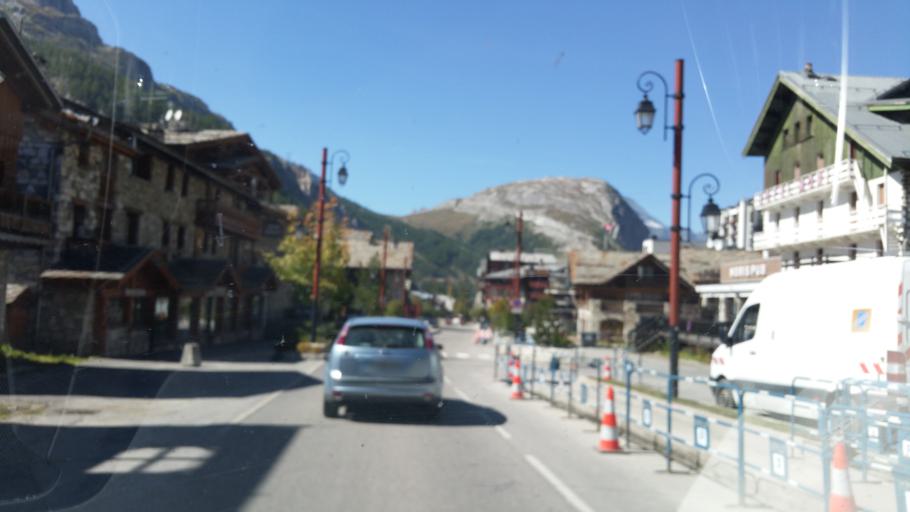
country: FR
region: Rhone-Alpes
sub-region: Departement de la Savoie
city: Val-d'Isere
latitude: 45.4482
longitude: 6.9820
